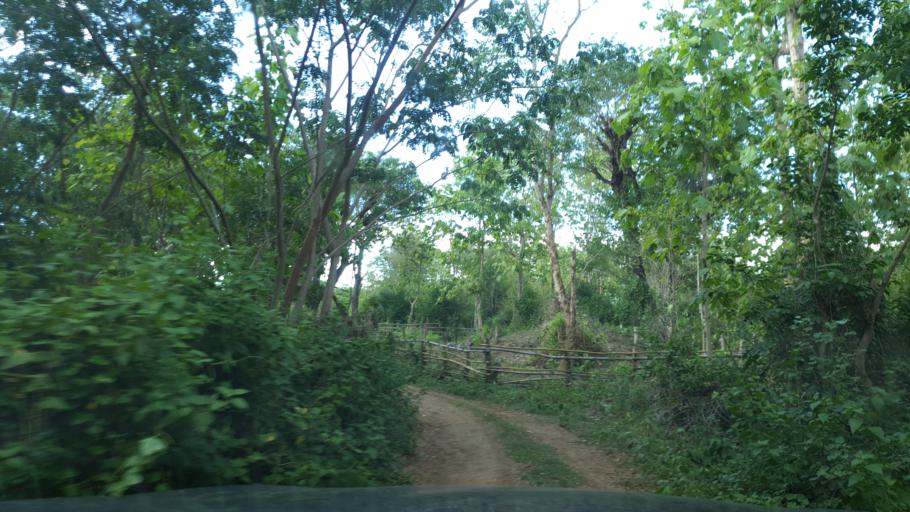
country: TH
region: Lampang
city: Sop Prap
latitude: 17.8851
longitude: 99.2904
